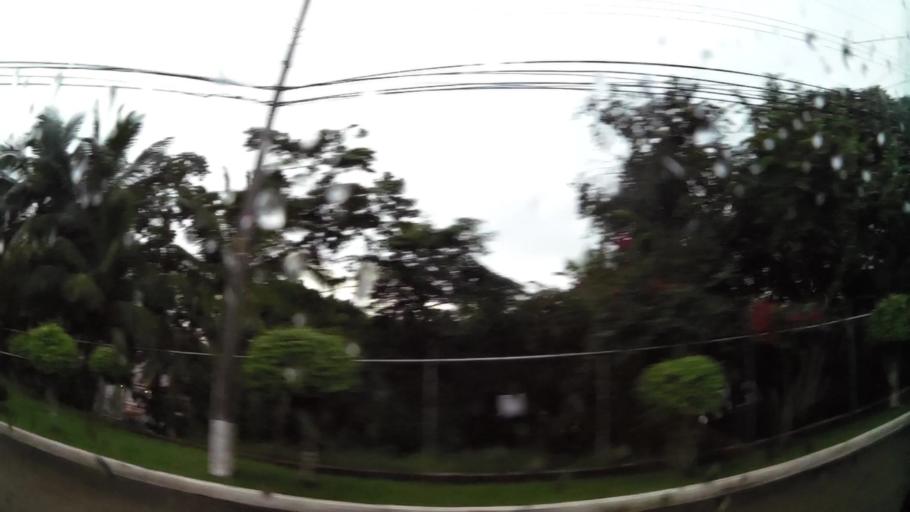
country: PA
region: Panama
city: Las Cumbres
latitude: 9.0423
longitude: -79.5274
